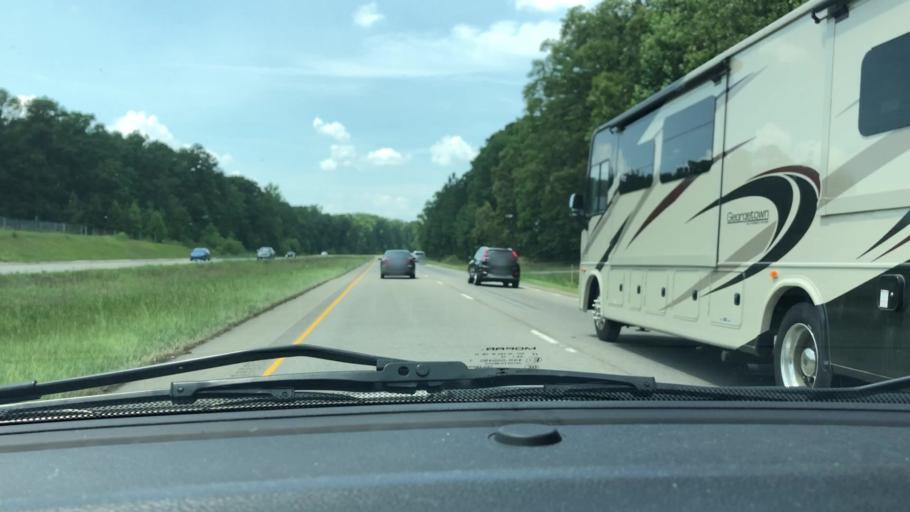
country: US
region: North Carolina
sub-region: Chatham County
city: Farmville
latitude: 35.5697
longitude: -79.3029
